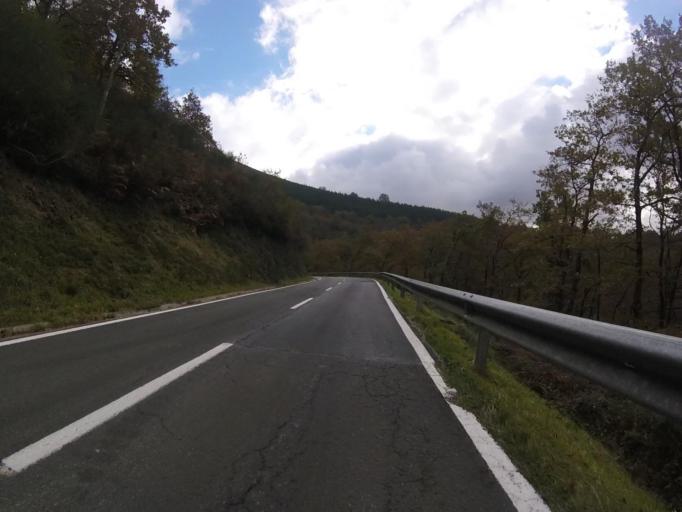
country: ES
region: Navarre
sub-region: Provincia de Navarra
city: Goizueta
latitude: 43.2070
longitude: -1.8578
